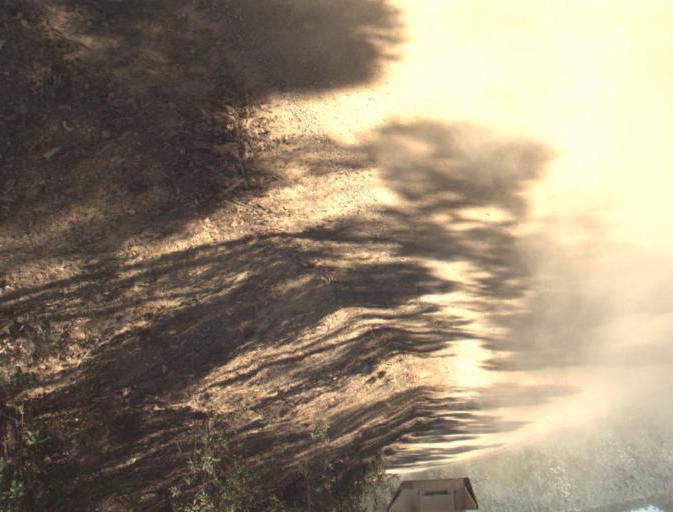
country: AU
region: Tasmania
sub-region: Launceston
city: Mayfield
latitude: -41.2238
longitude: 147.2483
